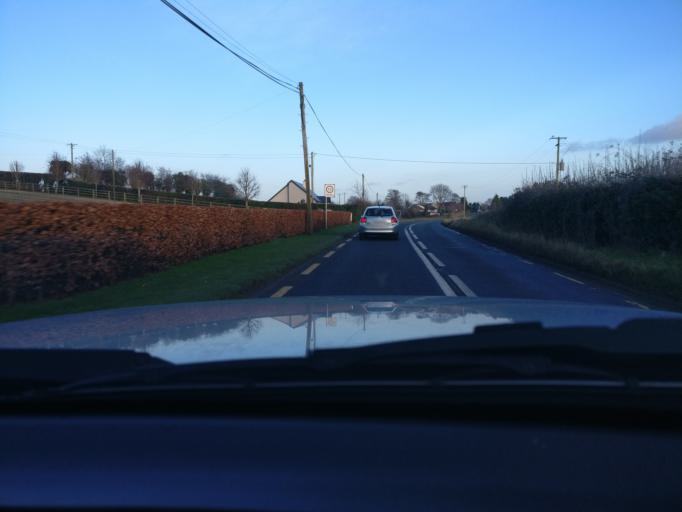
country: IE
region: Leinster
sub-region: Lu
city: Ardee
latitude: 53.8554
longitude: -6.5669
